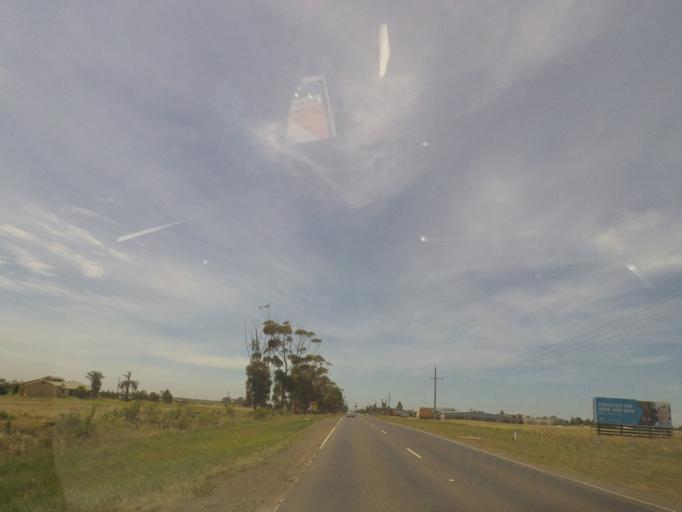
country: AU
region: Victoria
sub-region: Wyndham
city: Tarneit
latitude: -37.8729
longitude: 144.6137
